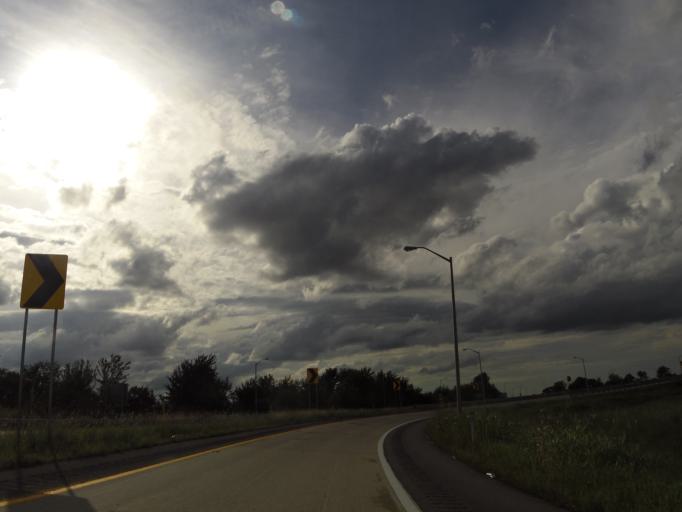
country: US
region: Kentucky
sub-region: Christian County
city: Oak Grove
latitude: 36.7013
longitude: -87.4564
